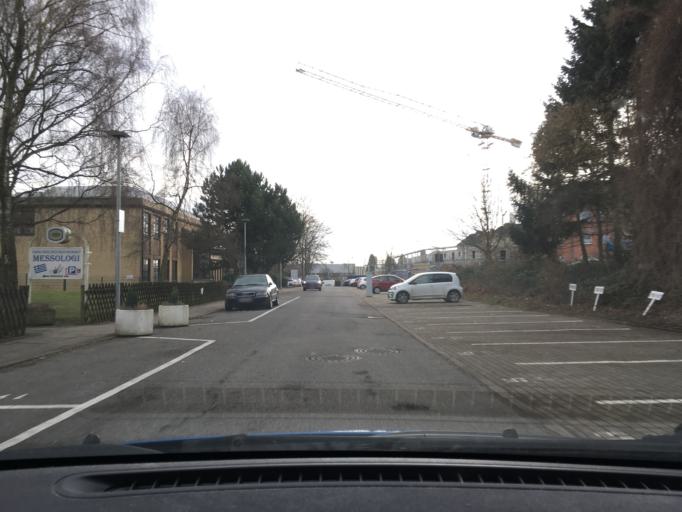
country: DE
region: Schleswig-Holstein
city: Wedel
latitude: 53.5794
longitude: 9.7272
